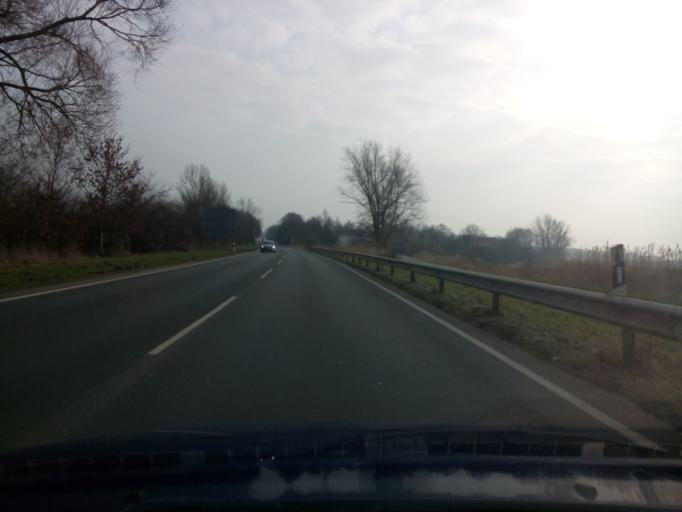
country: DE
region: Lower Saxony
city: Loxstedt
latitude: 53.4603
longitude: 8.6034
